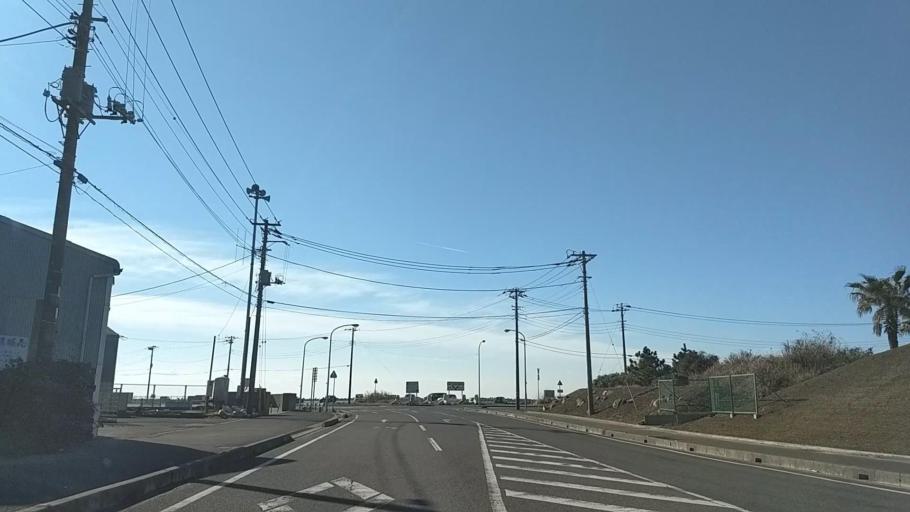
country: JP
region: Chiba
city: Hasaki
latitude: 35.7046
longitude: 140.8444
